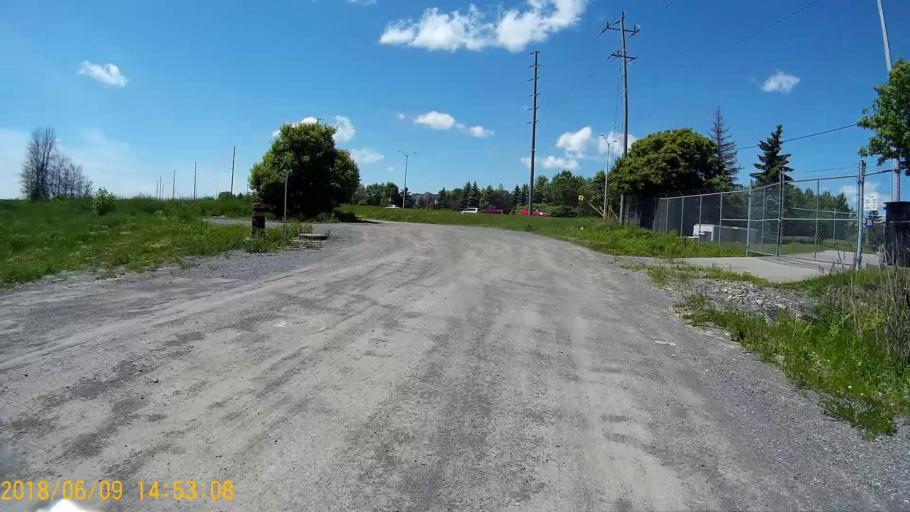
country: CA
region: Ontario
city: Bells Corners
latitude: 45.3092
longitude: -75.9223
